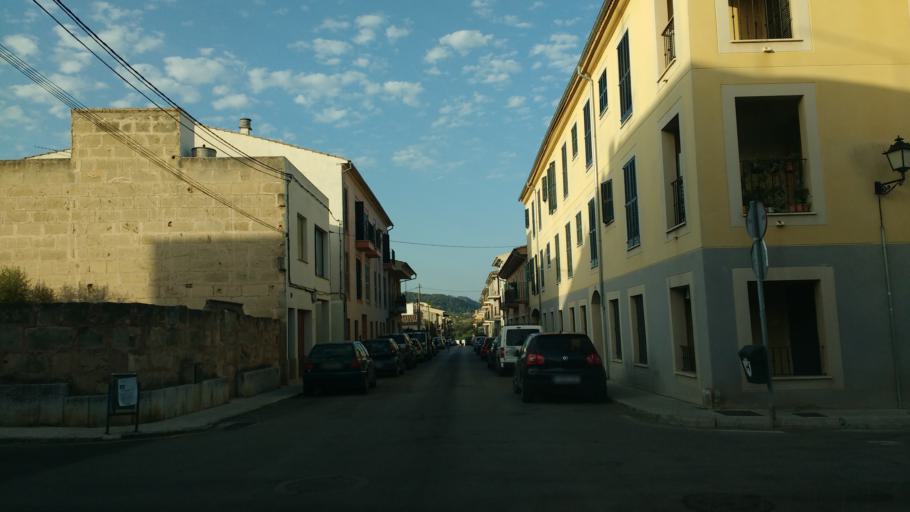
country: ES
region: Balearic Islands
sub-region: Illes Balears
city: Alaro
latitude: 39.7047
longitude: 2.7947
